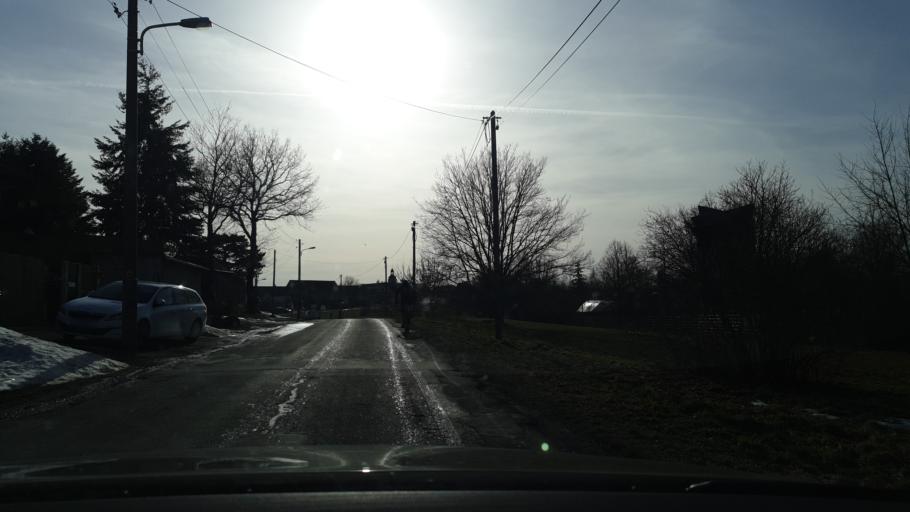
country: DE
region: Thuringia
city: Zedlitz
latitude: 50.8382
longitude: 12.0695
